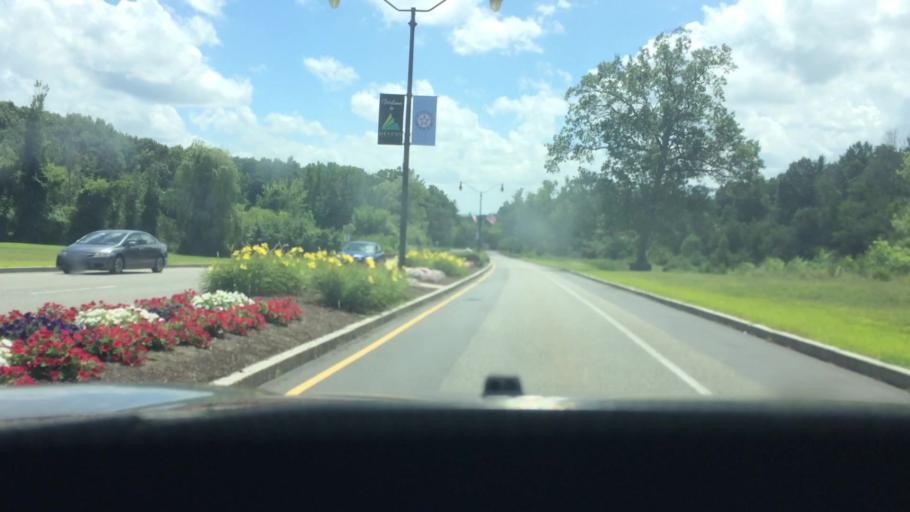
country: US
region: Massachusetts
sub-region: Middlesex County
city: Shirley
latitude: 42.5281
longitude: -71.6302
